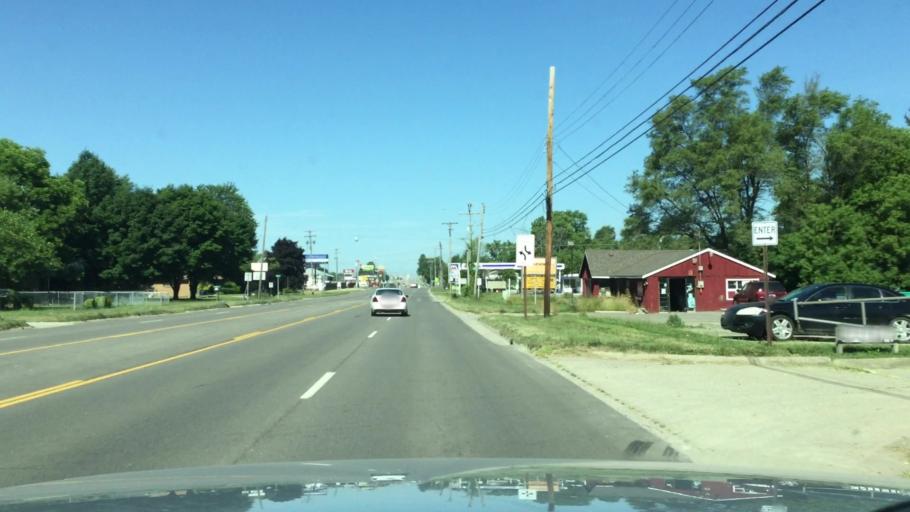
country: US
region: Michigan
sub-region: Genesee County
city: Beecher
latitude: 43.0608
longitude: -83.7470
